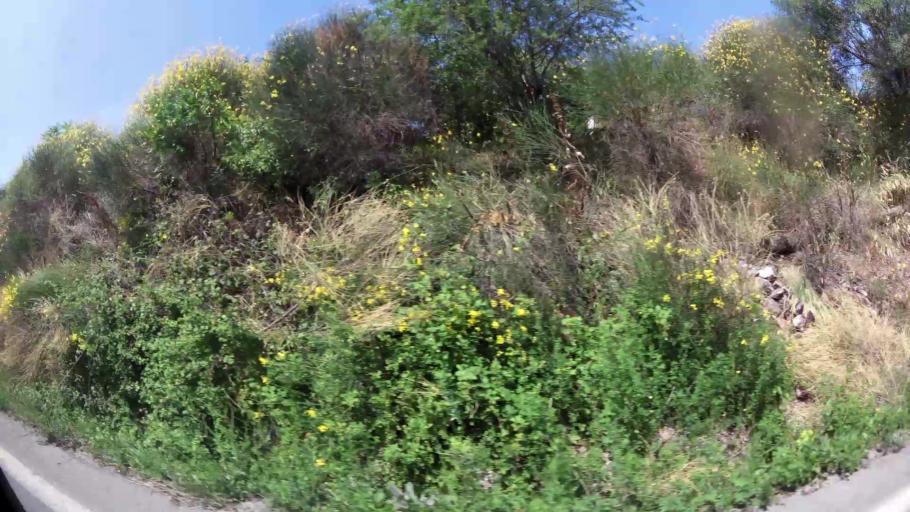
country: GR
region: West Macedonia
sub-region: Nomos Kozanis
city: Koila
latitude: 40.3208
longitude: 21.7881
